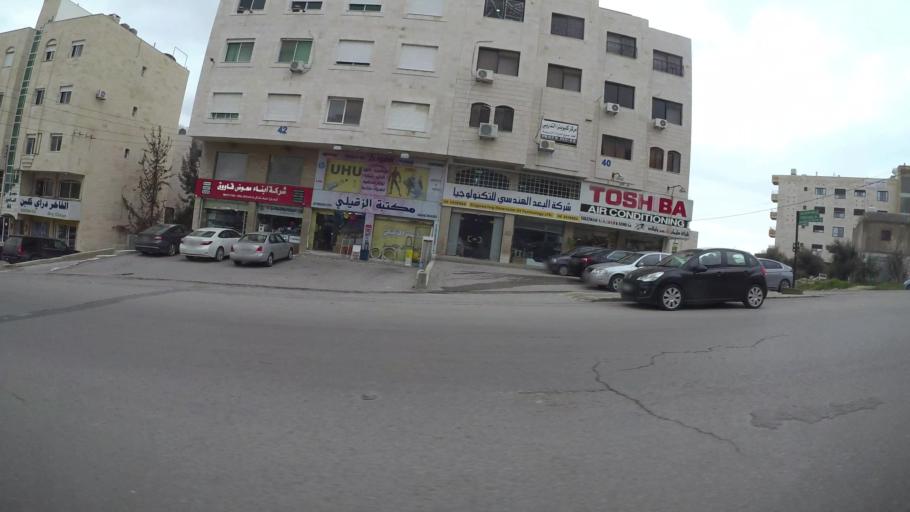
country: JO
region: Amman
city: Al Jubayhah
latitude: 31.9884
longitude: 35.8488
